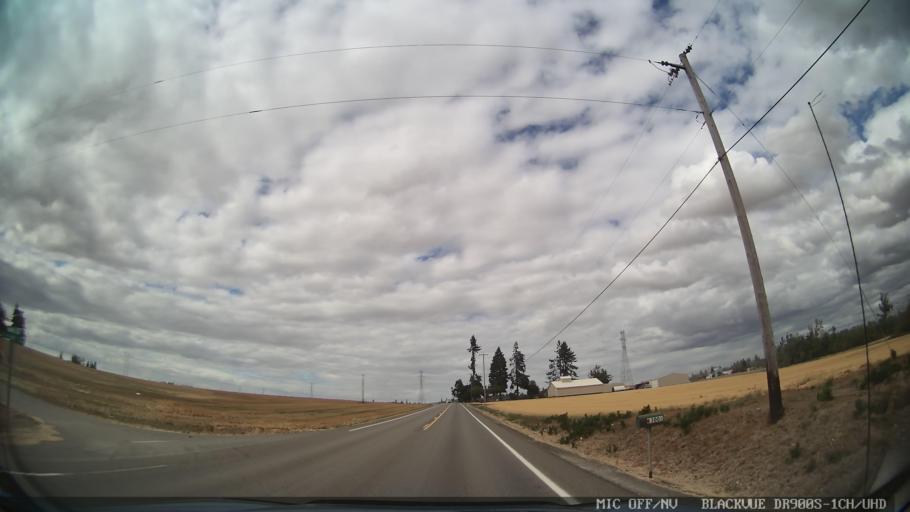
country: US
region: Oregon
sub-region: Marion County
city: Sublimity
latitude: 44.8613
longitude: -122.7926
